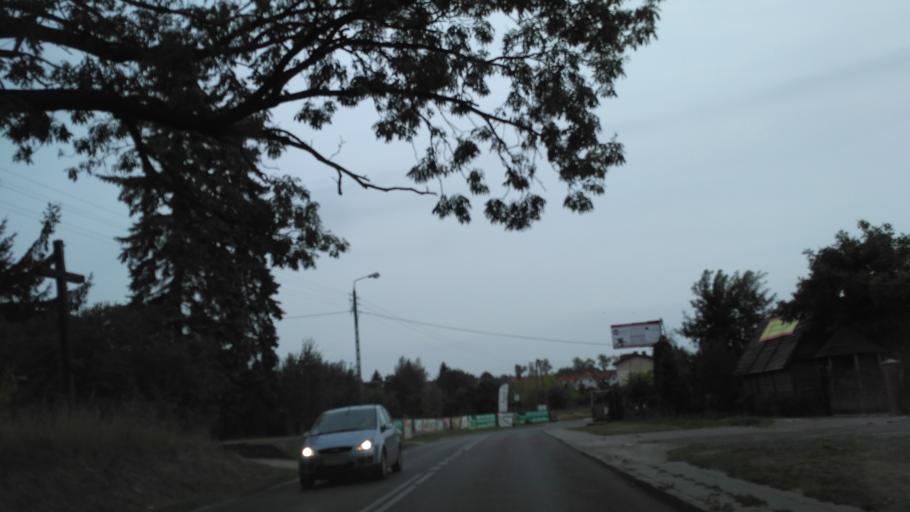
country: PL
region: Lublin Voivodeship
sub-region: Powiat lubelski
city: Lublin
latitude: 51.2085
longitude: 22.5978
